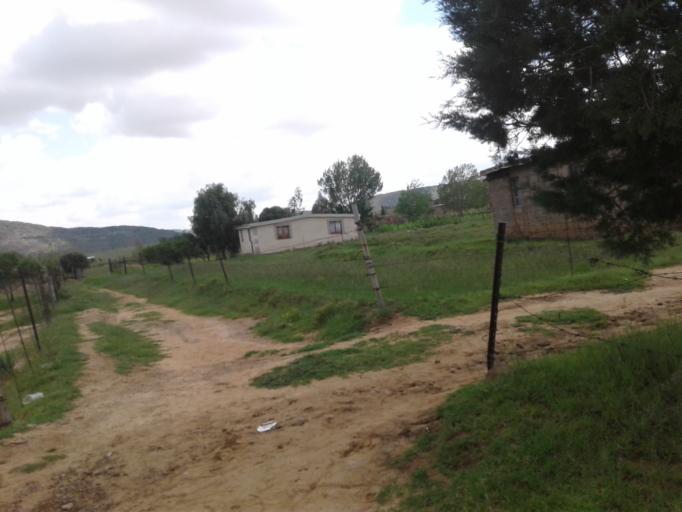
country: LS
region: Mafeteng
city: Mafeteng
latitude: -29.7504
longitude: 27.1112
